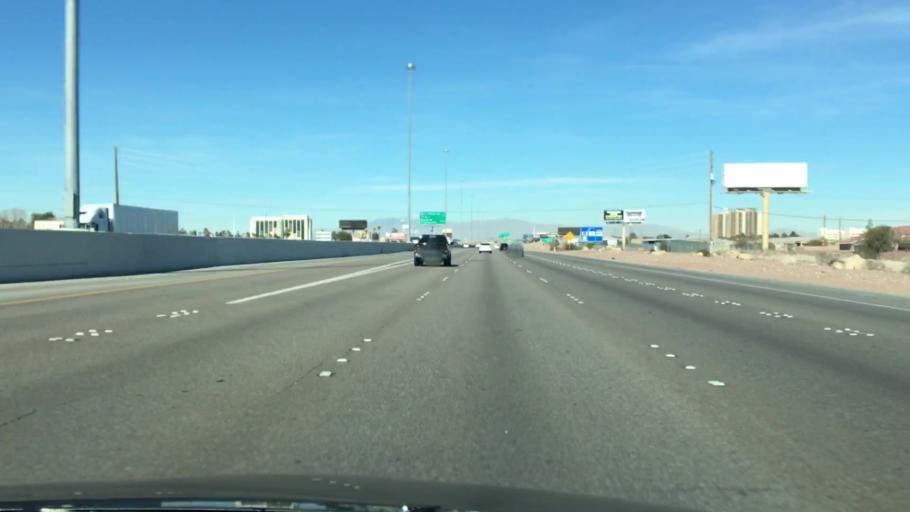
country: US
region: Nevada
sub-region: Clark County
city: Enterprise
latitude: 36.0253
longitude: -115.1806
